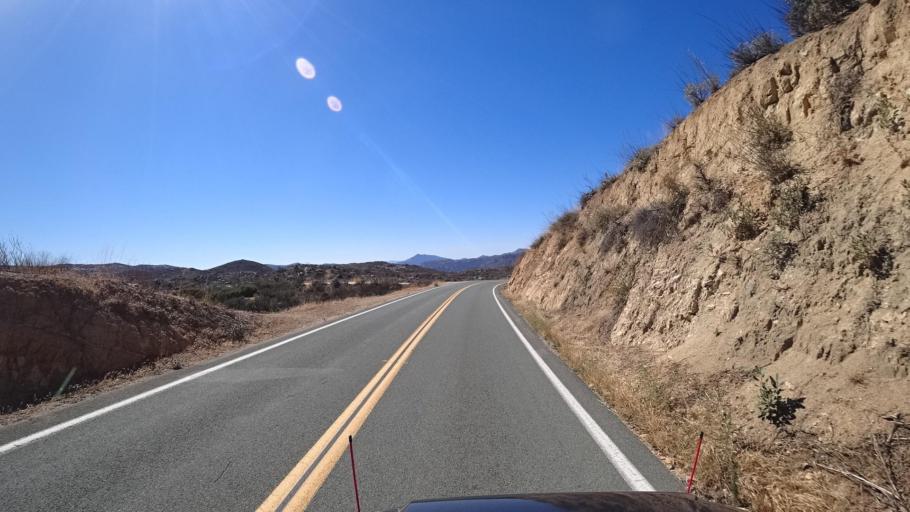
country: US
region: California
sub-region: San Diego County
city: Descanso
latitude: 32.7486
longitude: -116.6677
